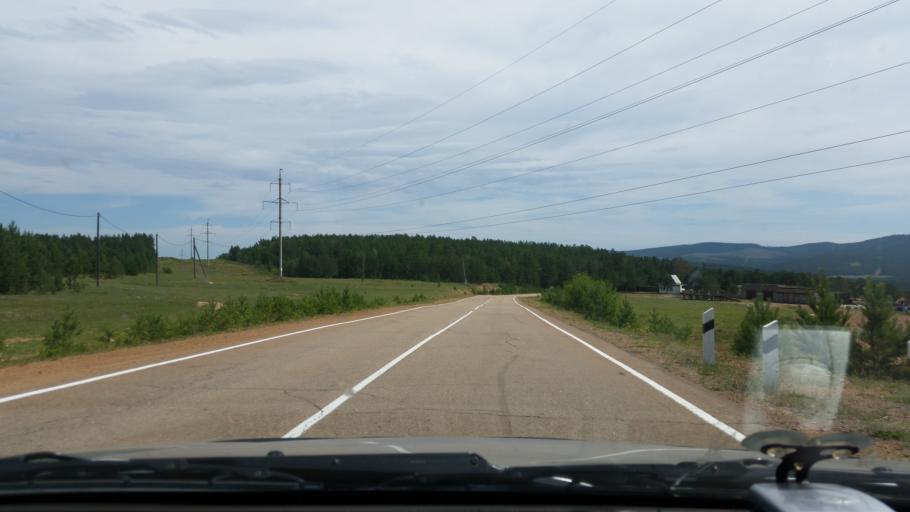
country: RU
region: Irkutsk
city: Yelantsy
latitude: 52.7620
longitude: 106.3189
